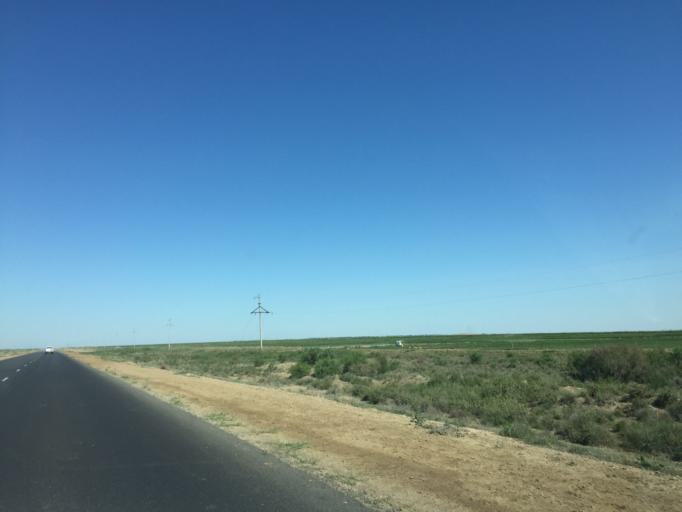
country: KZ
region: Qyzylorda
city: Dzhalagash
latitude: 44.9375
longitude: 64.6417
